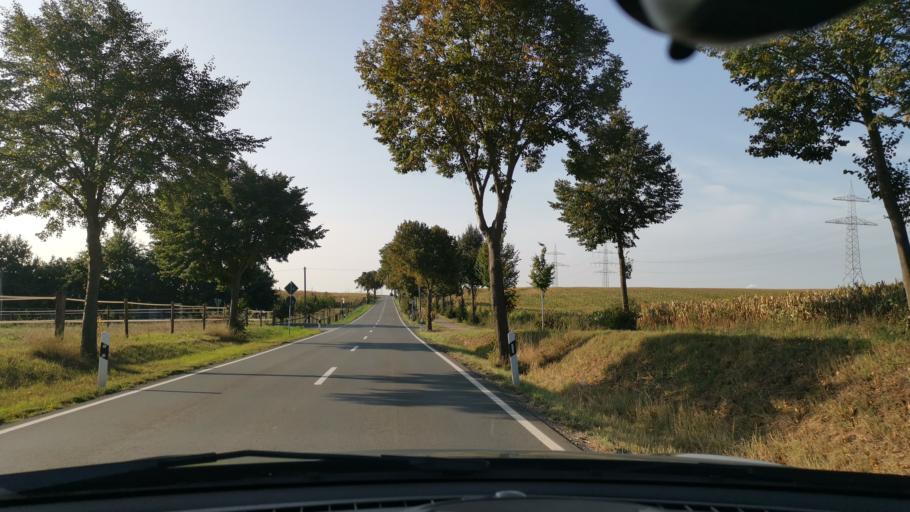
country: DE
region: North Rhine-Westphalia
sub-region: Regierungsbezirk Dusseldorf
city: Rommerskirchen
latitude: 51.0790
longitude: 6.7202
